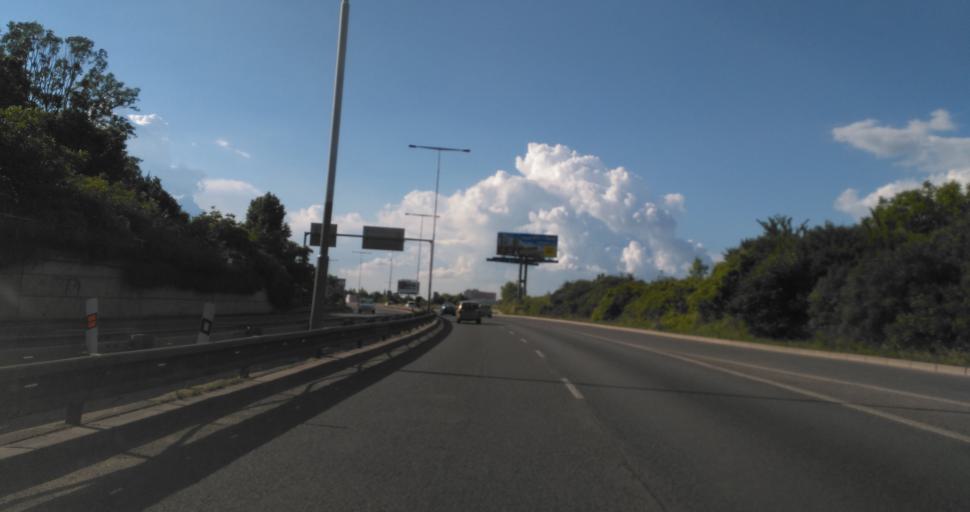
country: CZ
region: Praha
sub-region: Praha 9
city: Vysocany
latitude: 50.1200
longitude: 14.5170
